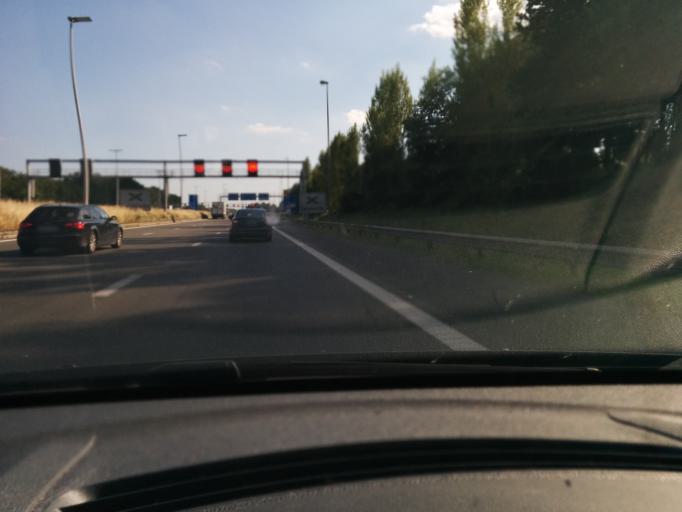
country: BE
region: Flanders
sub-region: Provincie Oost-Vlaanderen
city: Ledeberg
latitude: 51.0196
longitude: 3.7316
